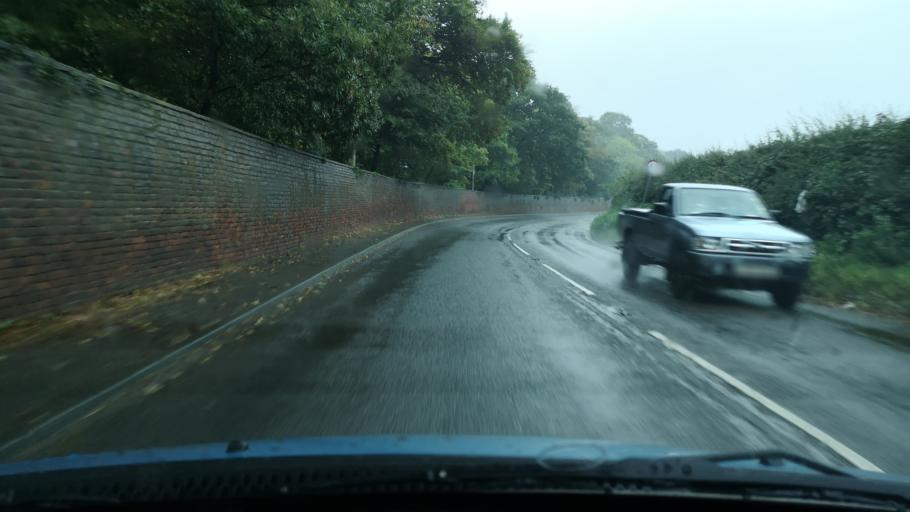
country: GB
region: England
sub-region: City and Borough of Wakefield
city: Sharlston
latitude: 53.6536
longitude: -1.3955
